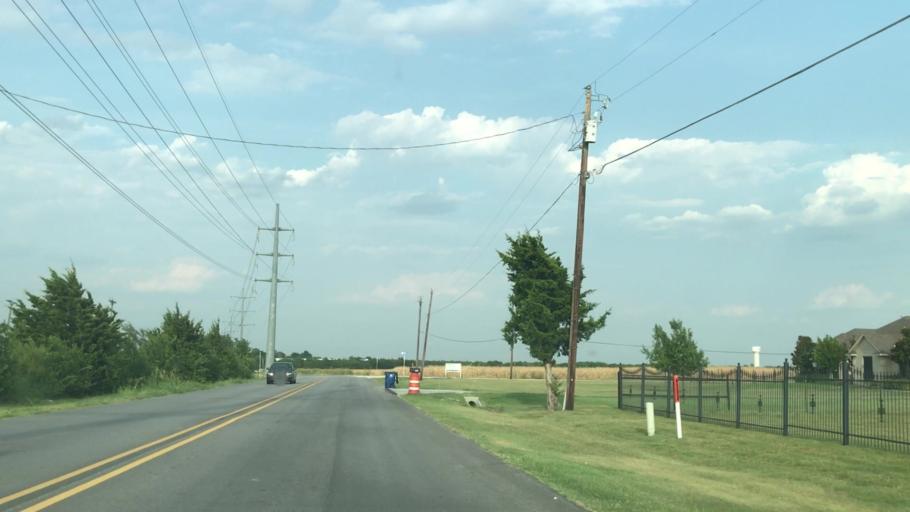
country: US
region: Texas
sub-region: Rockwall County
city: Fate
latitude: 32.9362
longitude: -96.4021
